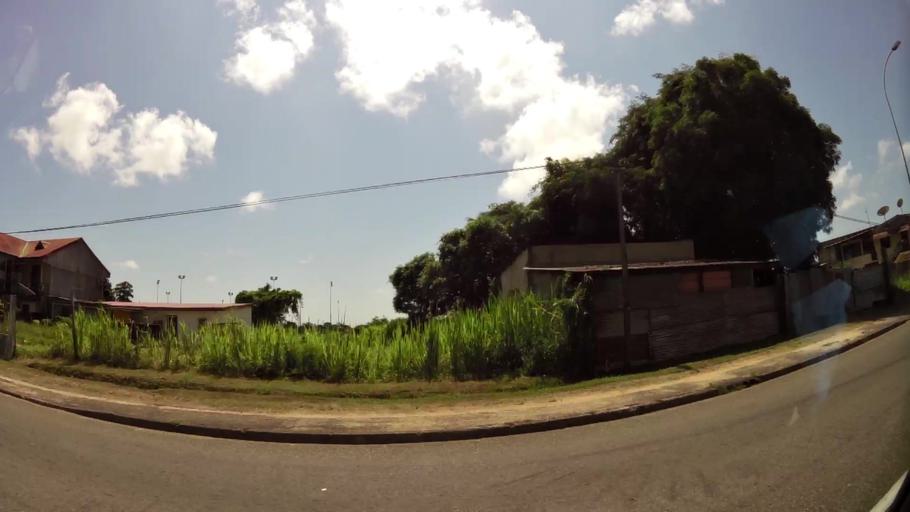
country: GF
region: Guyane
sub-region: Guyane
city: Cayenne
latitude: 4.9288
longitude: -52.3254
